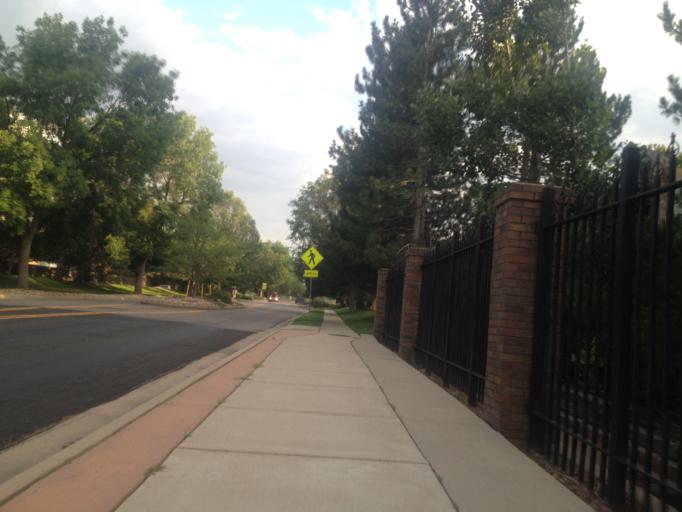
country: US
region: Colorado
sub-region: Boulder County
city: Boulder
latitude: 39.9888
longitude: -105.2236
